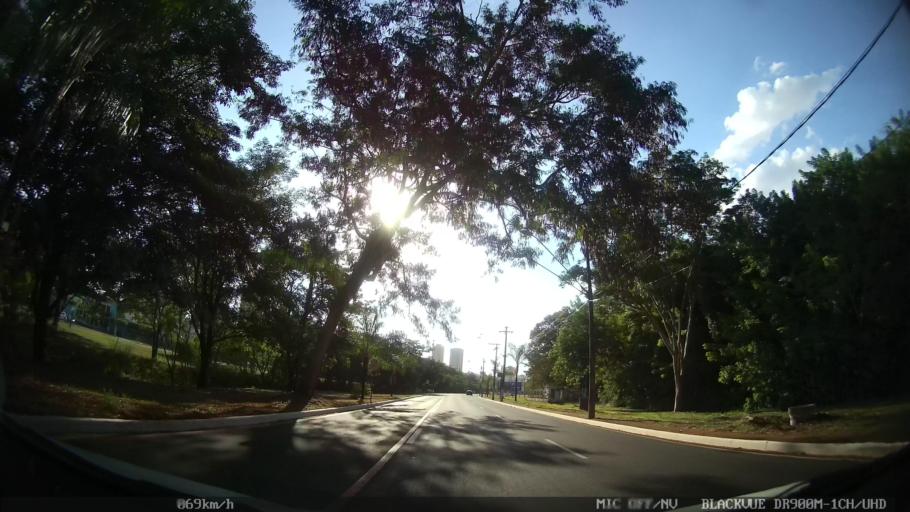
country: BR
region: Sao Paulo
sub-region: Ribeirao Preto
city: Ribeirao Preto
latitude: -21.2010
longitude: -47.7949
